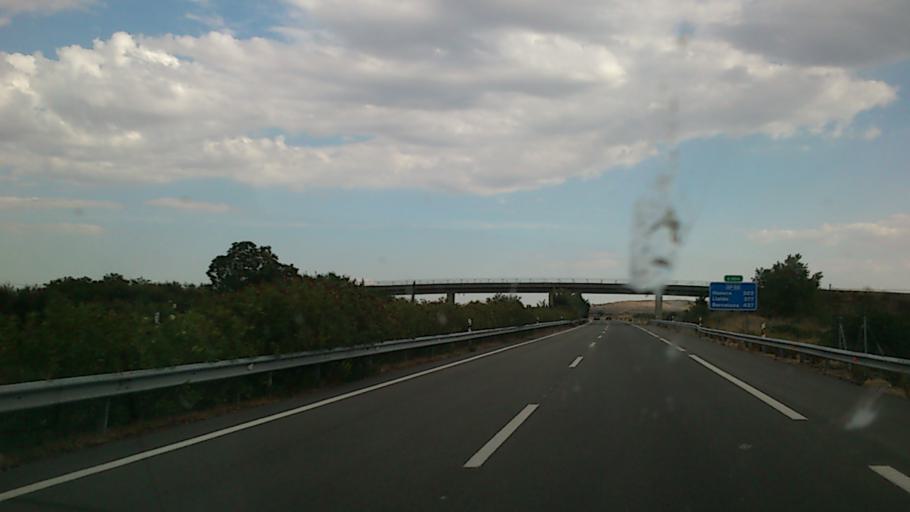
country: ES
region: La Rioja
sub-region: Provincia de La Rioja
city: Pradejon
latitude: 42.3479
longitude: -2.0483
